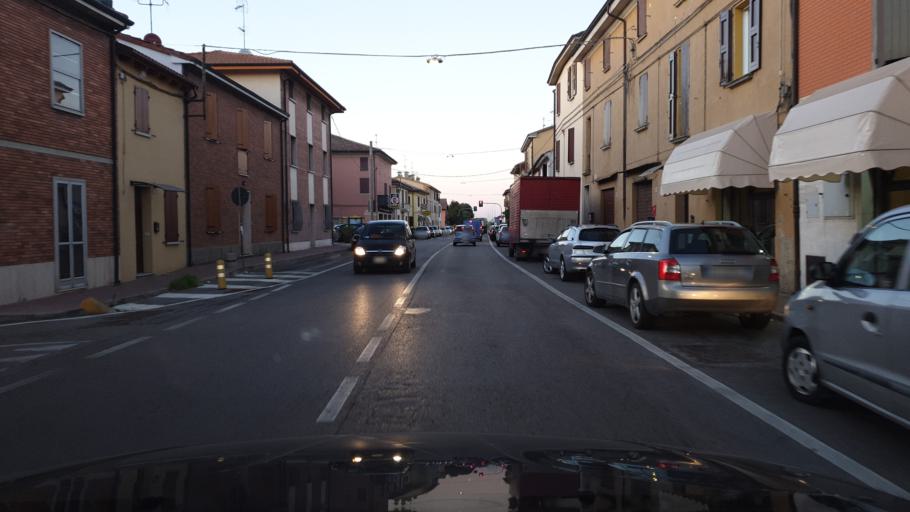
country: IT
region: Emilia-Romagna
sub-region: Provincia di Bologna
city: Ca De Fabbri
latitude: 44.6185
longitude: 11.4531
